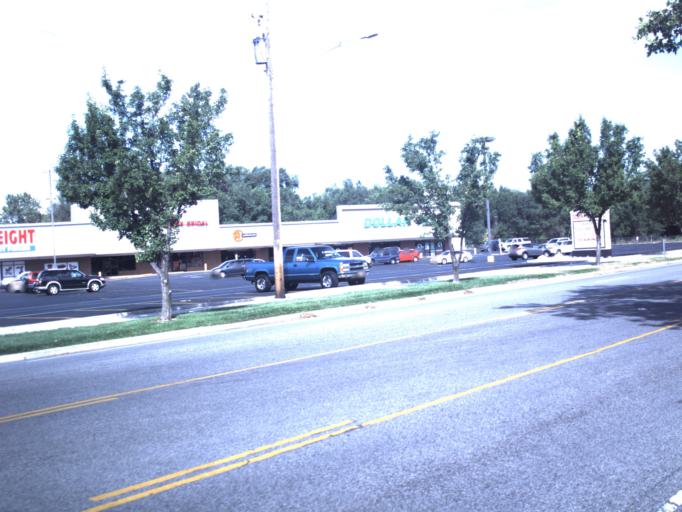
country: US
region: Utah
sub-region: Weber County
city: Harrisville
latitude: 41.2611
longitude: -111.9709
